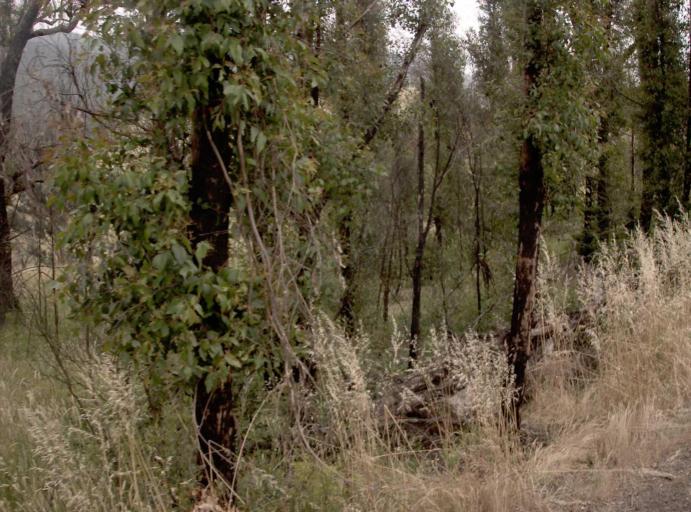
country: AU
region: Victoria
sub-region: Wellington
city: Heyfield
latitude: -37.8287
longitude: 146.6775
